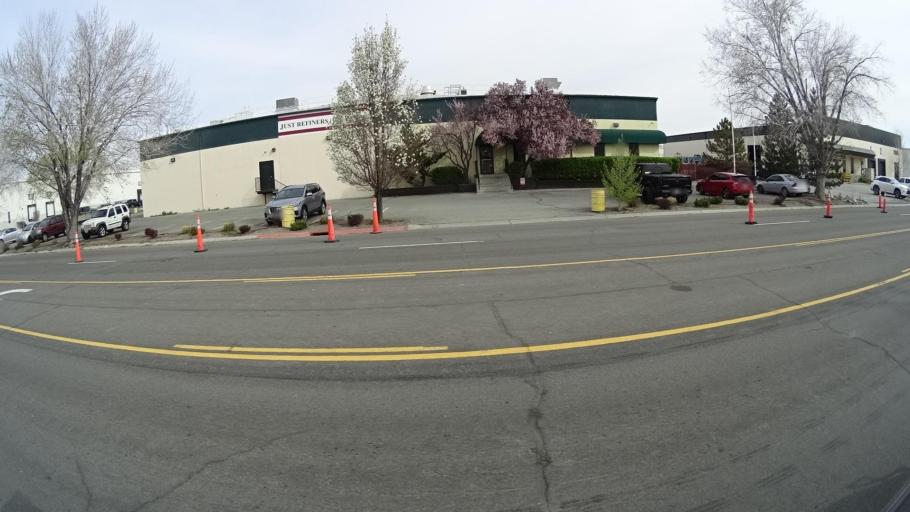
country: US
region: Nevada
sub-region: Washoe County
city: Sparks
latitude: 39.5215
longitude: -119.7504
